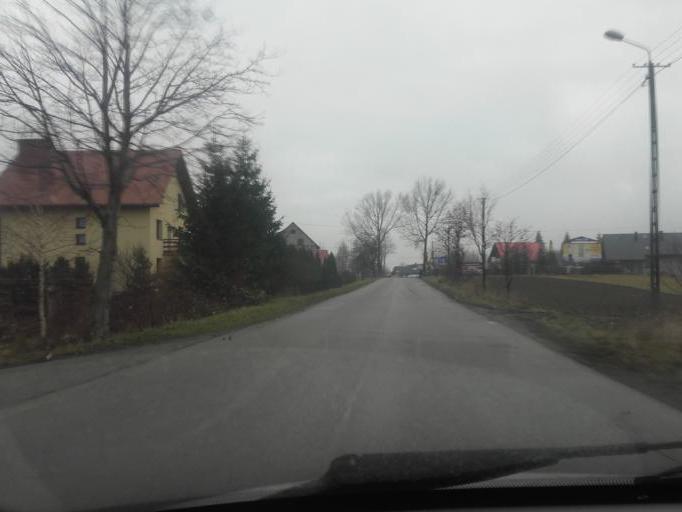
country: PL
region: Silesian Voivodeship
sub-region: Powiat cieszynski
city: Istebna
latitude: 49.5537
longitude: 18.9211
